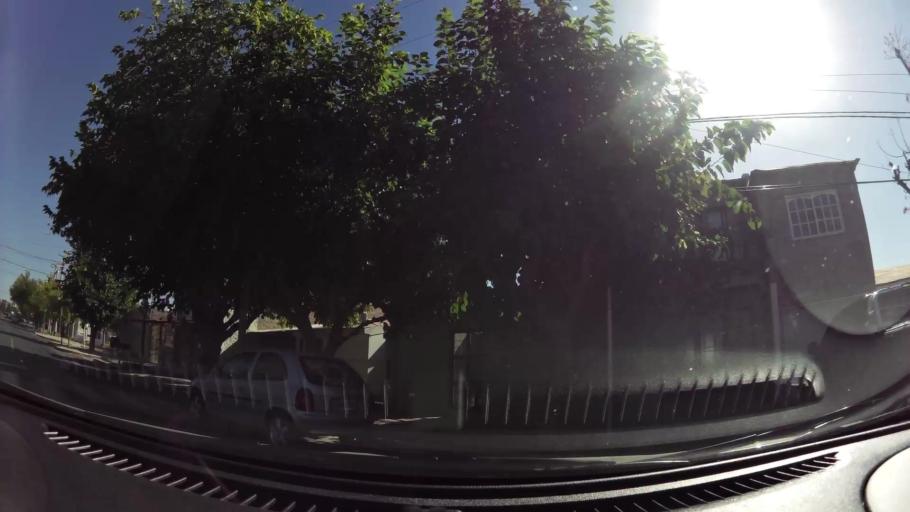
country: AR
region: Mendoza
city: Villa Nueva
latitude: -32.9121
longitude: -68.7974
